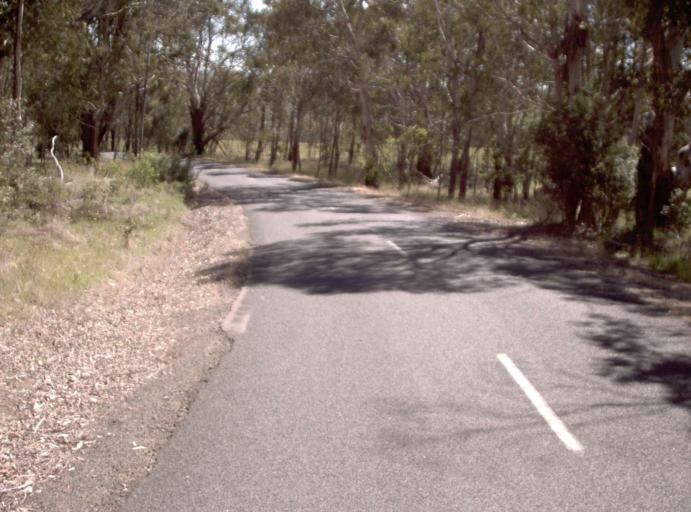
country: AU
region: New South Wales
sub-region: Bombala
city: Bombala
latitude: -37.0566
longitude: 148.8049
